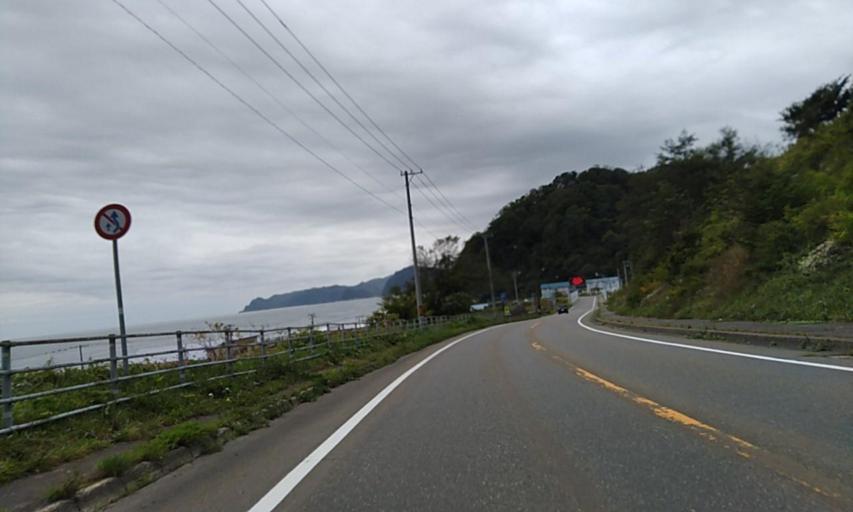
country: JP
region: Hokkaido
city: Obihiro
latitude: 42.2832
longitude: 143.3188
